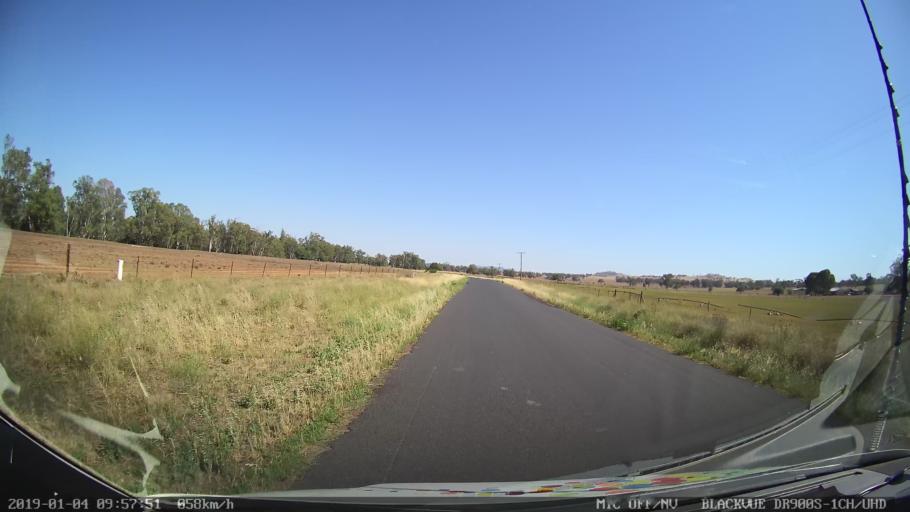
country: AU
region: New South Wales
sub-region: Cabonne
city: Canowindra
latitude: -33.5244
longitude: 148.3980
